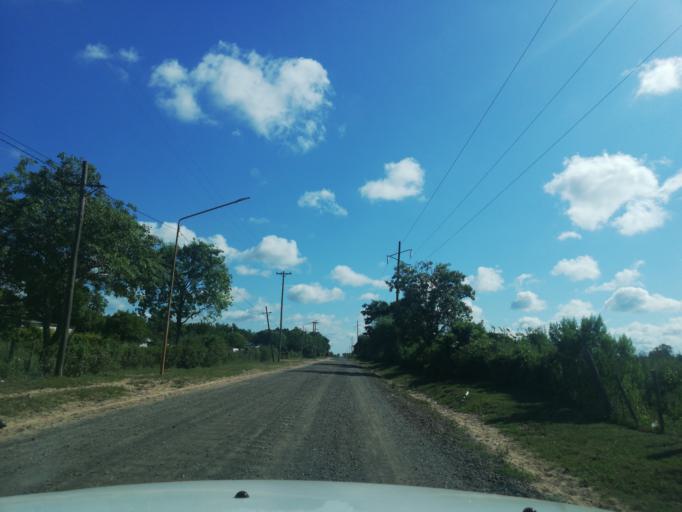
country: AR
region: Corrientes
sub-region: Departamento de San Miguel
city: San Miguel
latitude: -27.9885
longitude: -57.5864
